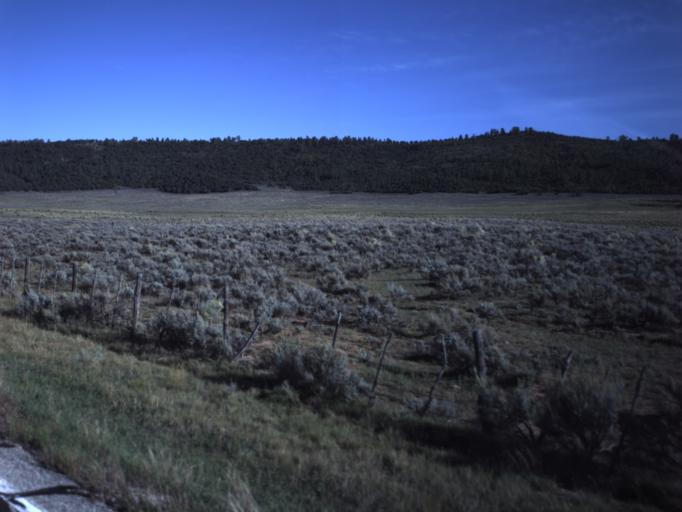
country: US
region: Utah
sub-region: Grand County
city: Moab
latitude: 38.3287
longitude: -109.1377
